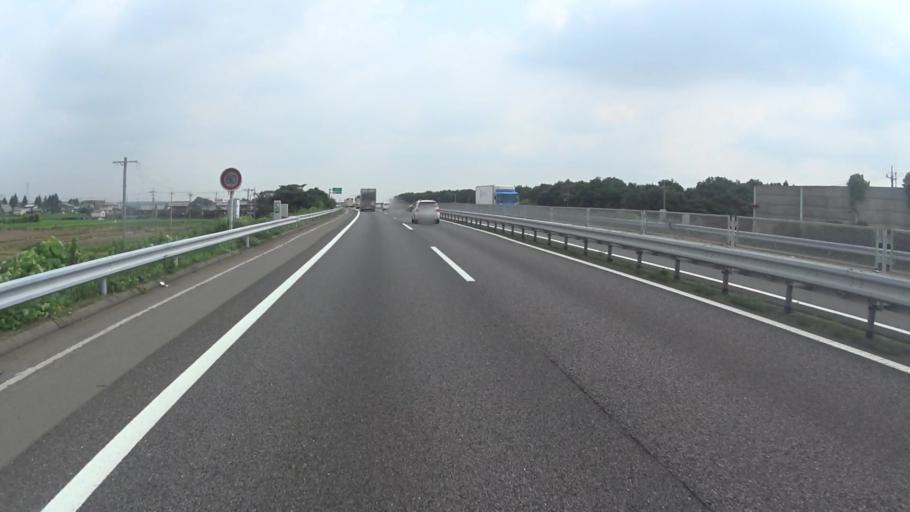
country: JP
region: Mie
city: Komono
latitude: 34.9241
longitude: 136.4859
